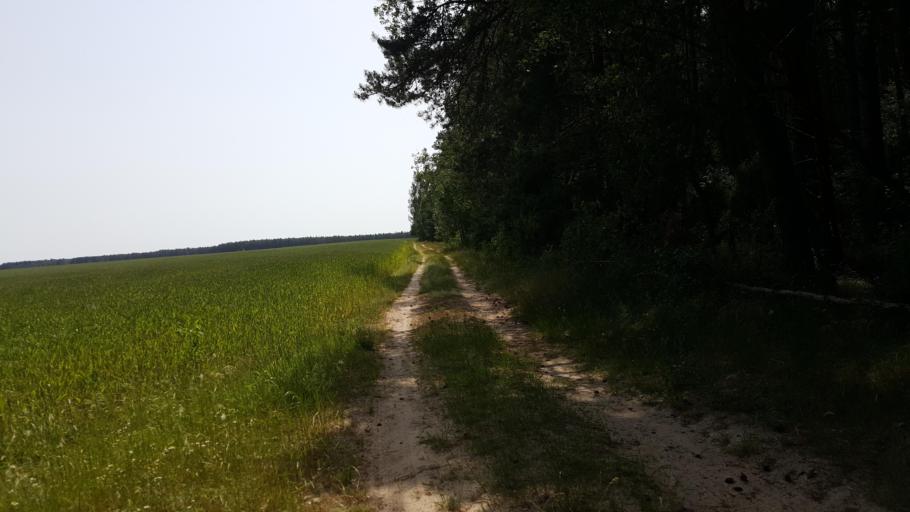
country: BY
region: Brest
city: Kamyanyets
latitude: 52.4764
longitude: 23.8384
